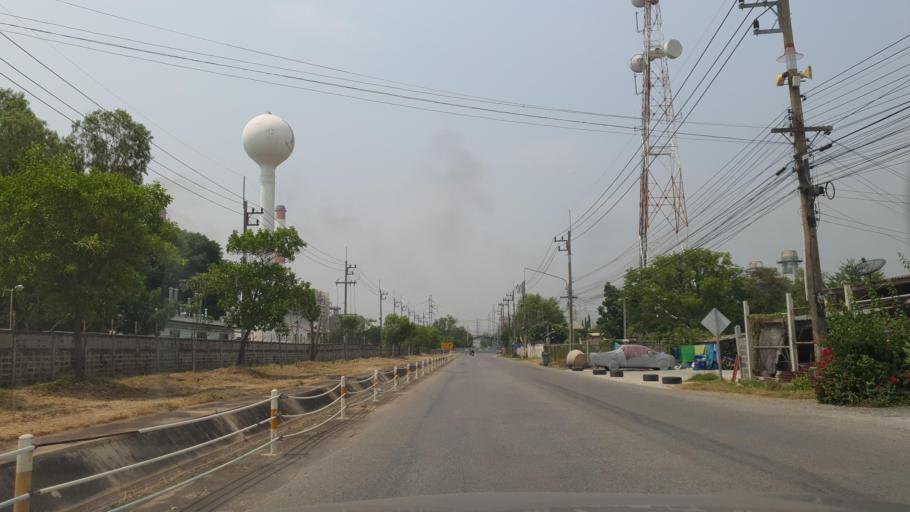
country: TH
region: Chachoengsao
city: Bang Pakong
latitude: 13.4956
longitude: 101.0281
